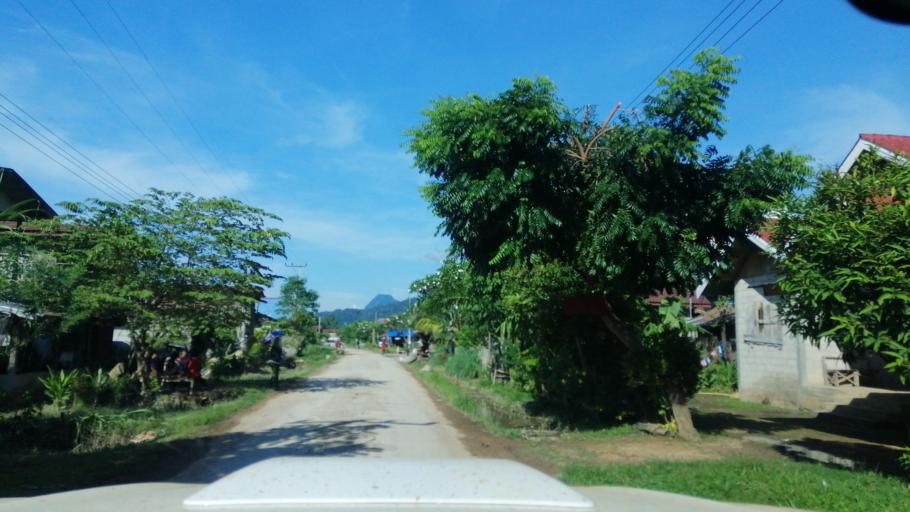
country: LA
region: Vientiane
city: Muang Sanakham
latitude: 18.3540
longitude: 101.5461
